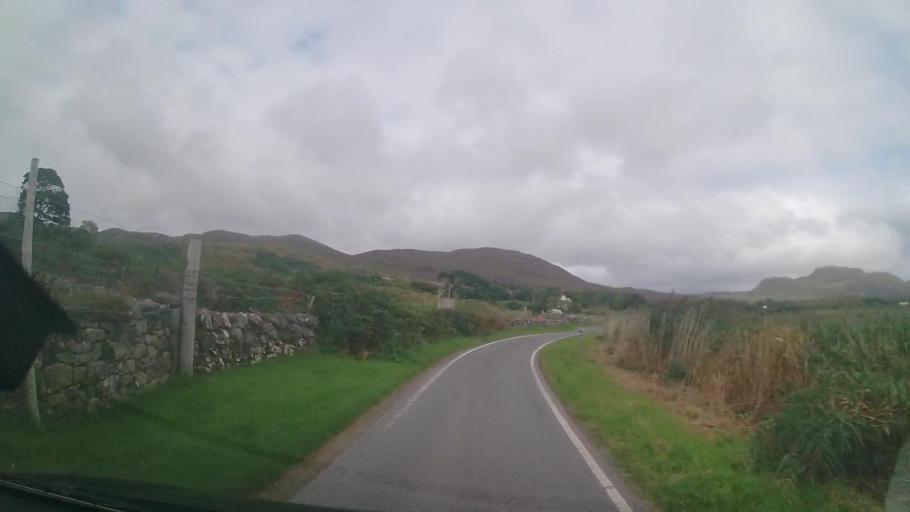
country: GB
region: Scotland
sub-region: Argyll and Bute
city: Isle Of Mull
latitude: 56.6964
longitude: -6.1188
